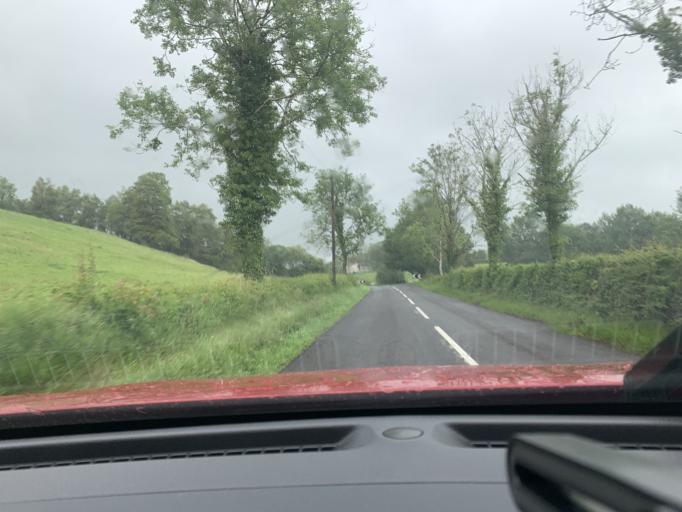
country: GB
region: Northern Ireland
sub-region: Fermanagh District
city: Enniskillen
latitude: 54.3048
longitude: -7.6874
